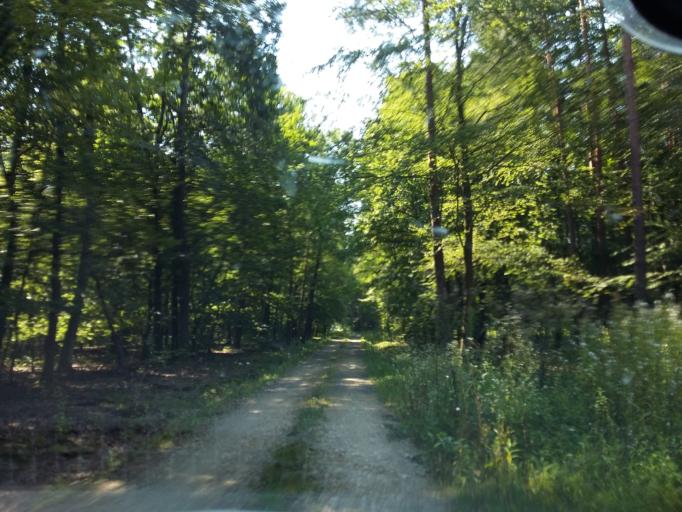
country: SI
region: Hodos-Hodos
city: Hodos
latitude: 46.8518
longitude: 16.3189
